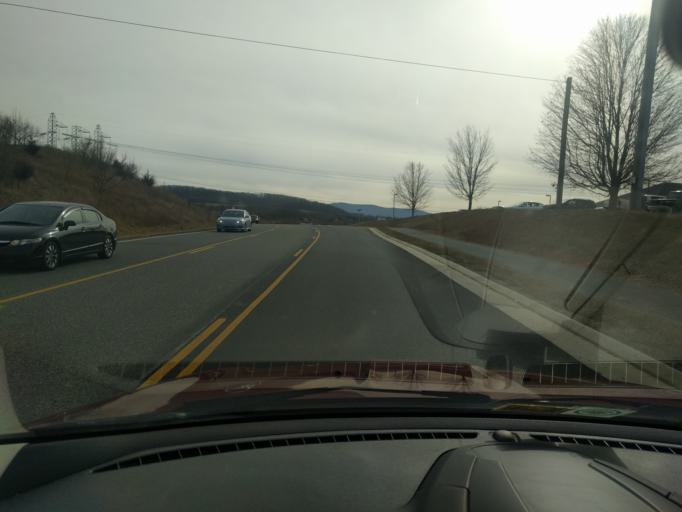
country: US
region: Virginia
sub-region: Augusta County
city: Fishersville
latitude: 38.0908
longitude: -78.9879
